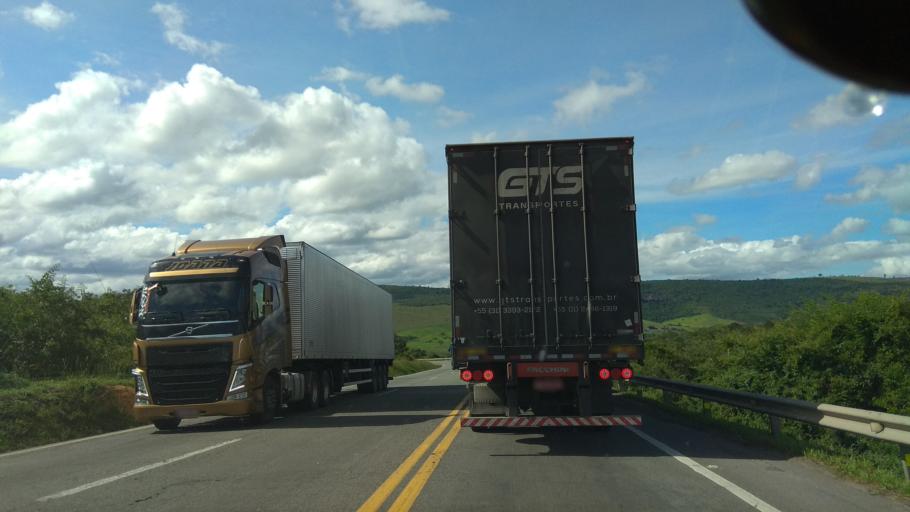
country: BR
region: Bahia
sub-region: Santa Ines
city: Santa Ines
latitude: -13.1750
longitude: -40.0013
